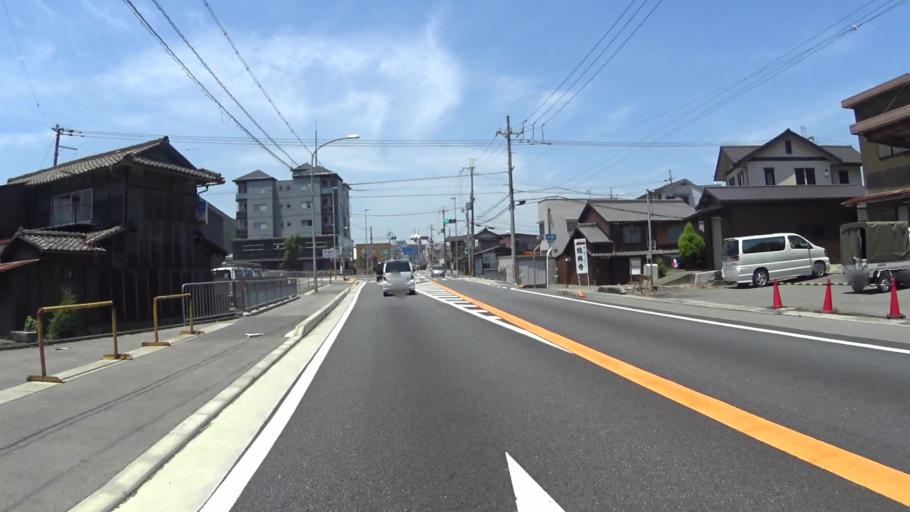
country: JP
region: Kyoto
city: Kameoka
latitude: 35.0682
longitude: 135.5352
